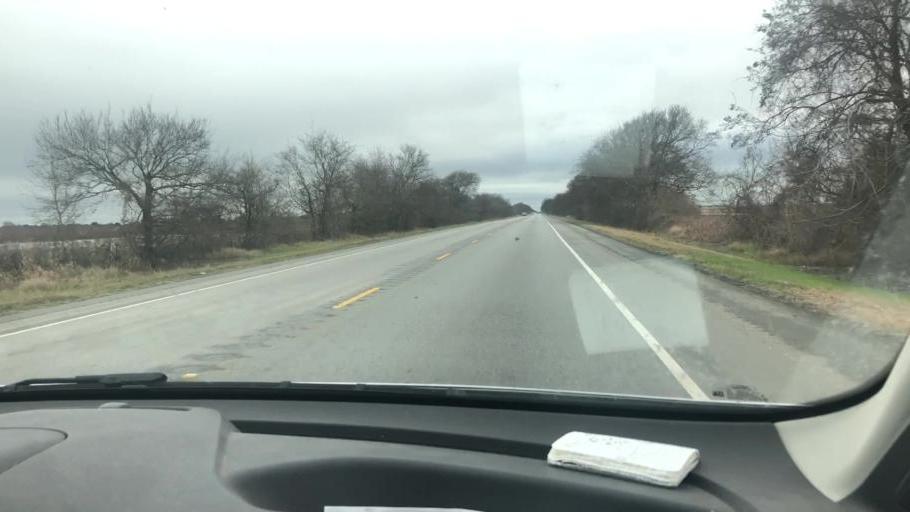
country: US
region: Texas
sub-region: Matagorda County
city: Van Vleck
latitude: 29.1172
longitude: -95.9803
